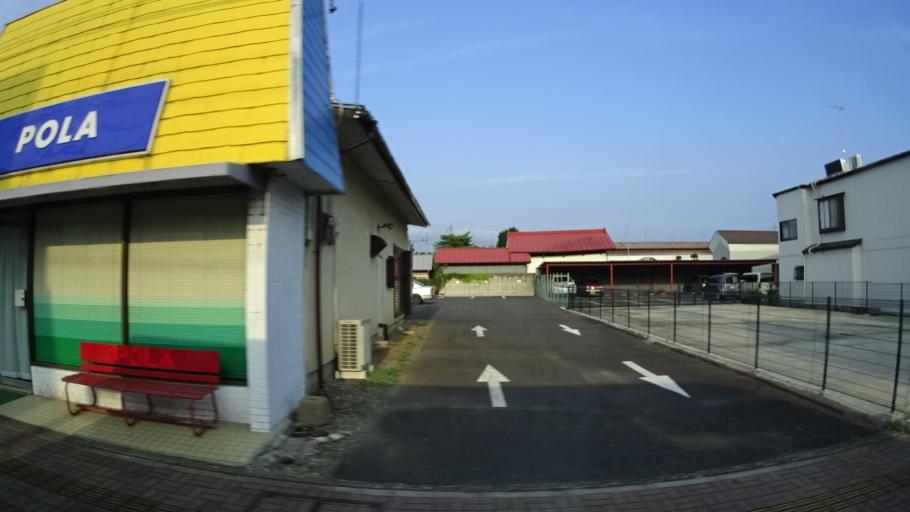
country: JP
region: Tochigi
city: Karasuyama
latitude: 36.6574
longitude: 140.1542
